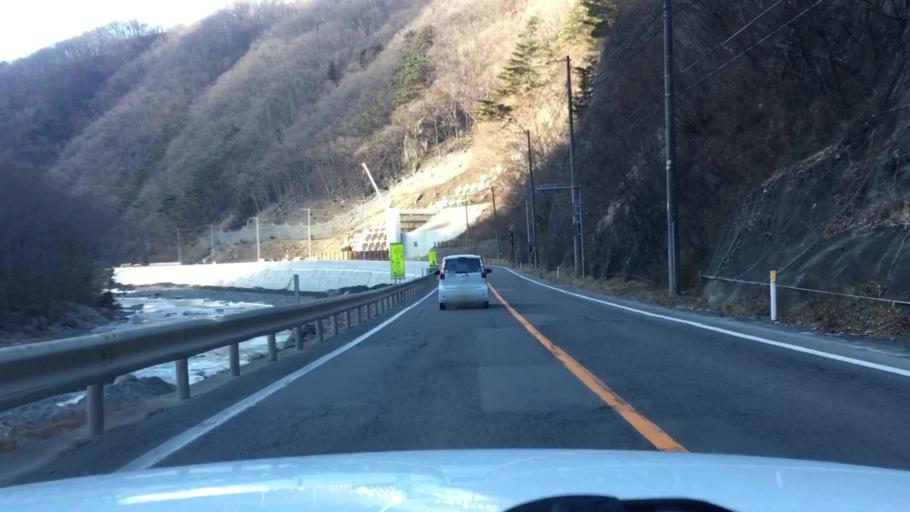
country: JP
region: Iwate
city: Miyako
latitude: 39.5977
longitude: 141.7592
